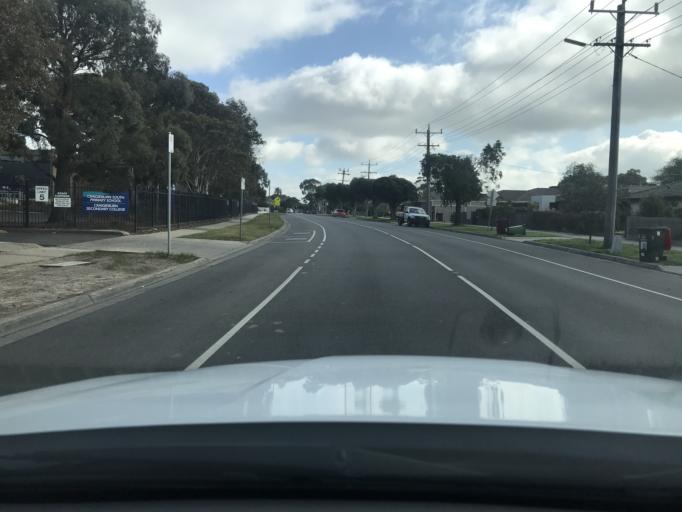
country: AU
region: Victoria
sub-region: Hume
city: Craigieburn
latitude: -37.6089
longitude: 144.9363
